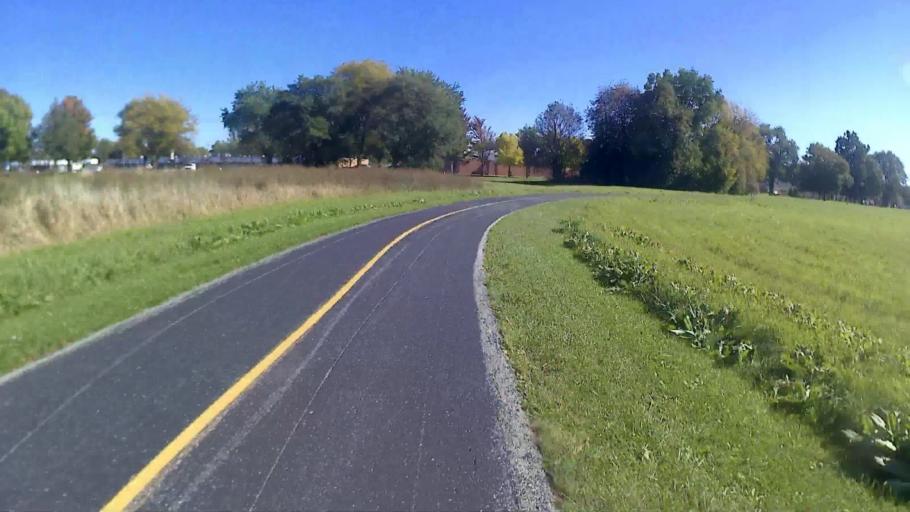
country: US
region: Illinois
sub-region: Cook County
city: Elk Grove Village
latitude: 42.0266
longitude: -87.9895
